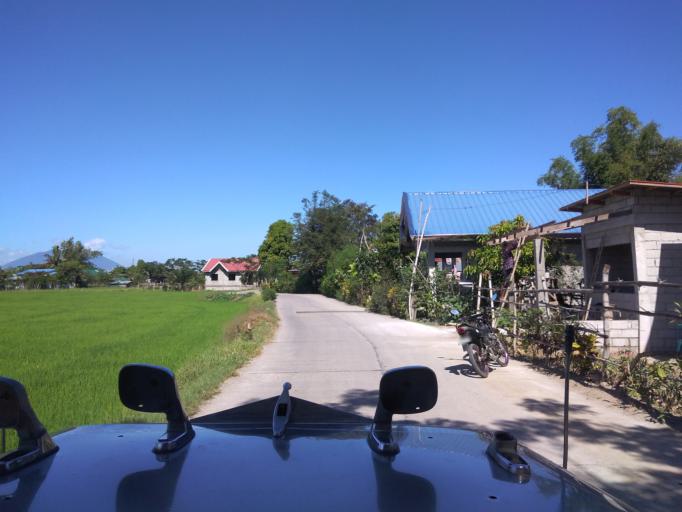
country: PH
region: Central Luzon
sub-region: Province of Pampanga
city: Batasan Bata
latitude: 15.1645
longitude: 120.9193
